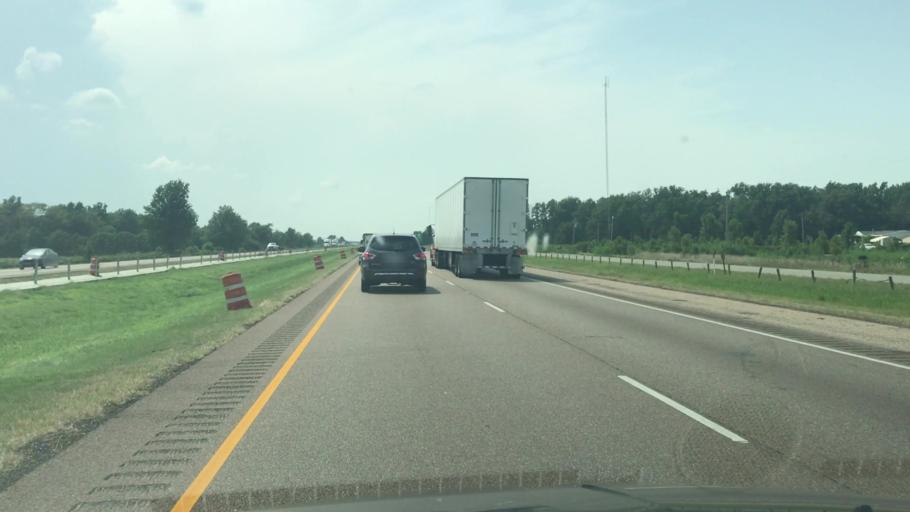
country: US
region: Arkansas
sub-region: Crittenden County
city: Earle
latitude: 35.1505
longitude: -90.3758
